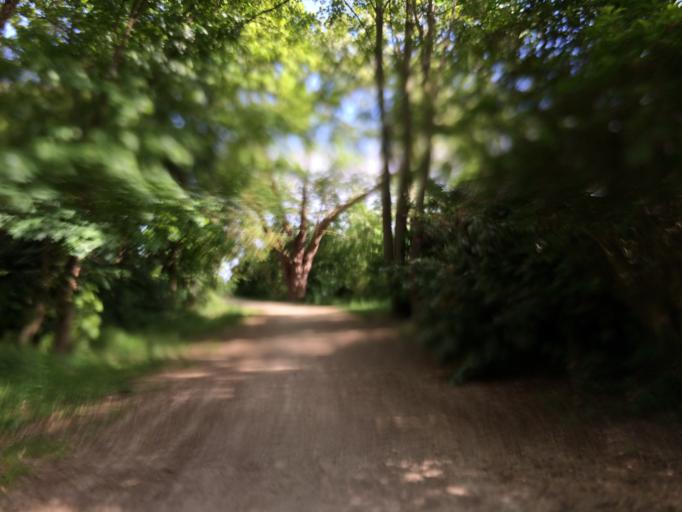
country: FR
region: Ile-de-France
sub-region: Departement de l'Essonne
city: Juvisy-sur-Orge
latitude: 48.6792
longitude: 2.3881
